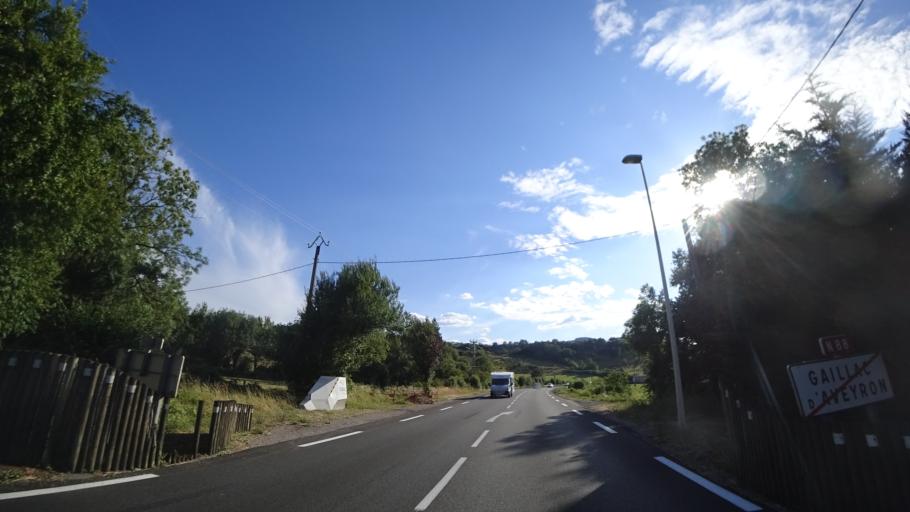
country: FR
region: Midi-Pyrenees
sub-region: Departement de l'Aveyron
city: Laissac
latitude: 44.3533
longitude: 2.9268
